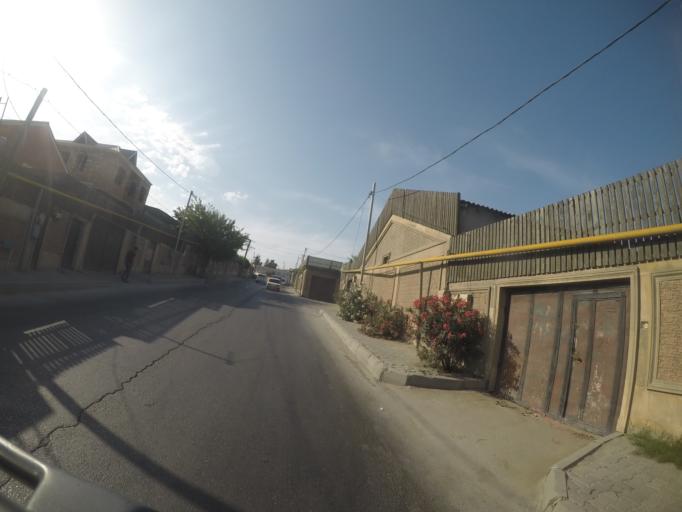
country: AZ
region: Baki
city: Binagadi
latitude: 40.4645
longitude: 49.8423
